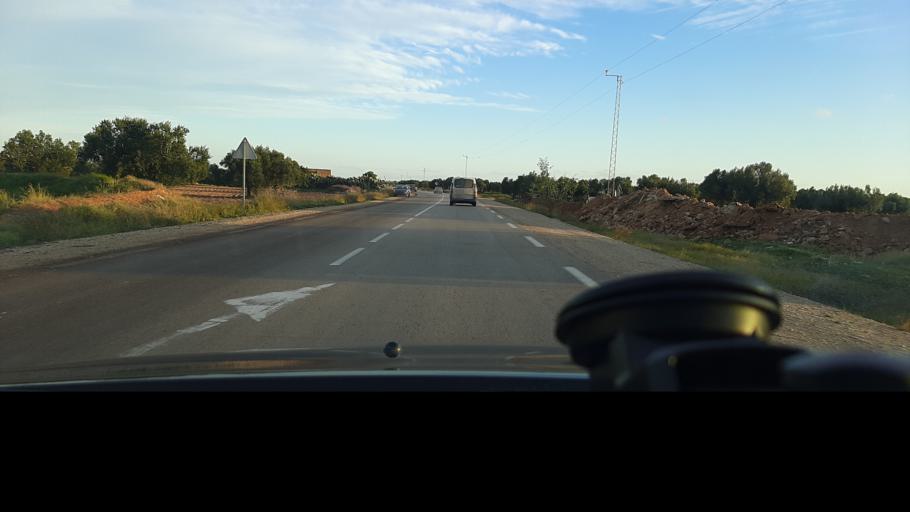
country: TN
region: Safaqis
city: Sfax
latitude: 34.9337
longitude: 10.6185
